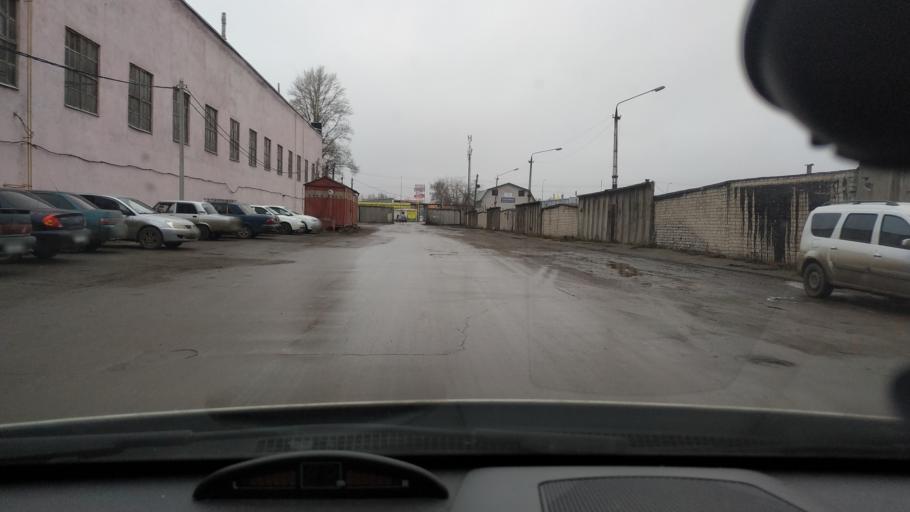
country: RU
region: Rjazan
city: Ryazan'
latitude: 54.6562
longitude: 39.6407
